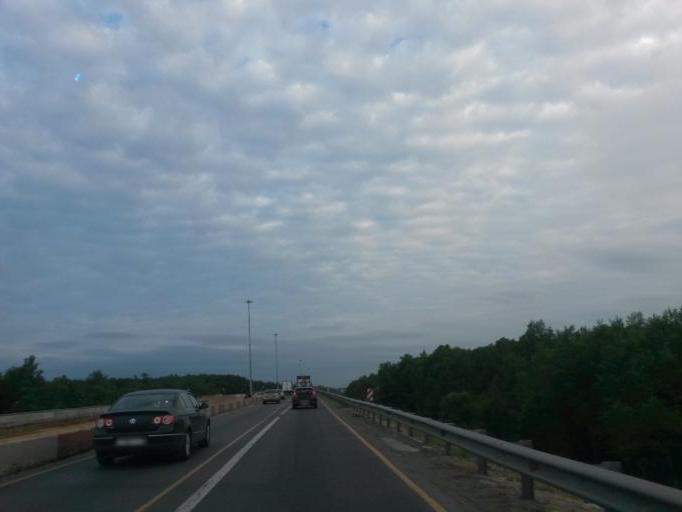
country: RU
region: Moskovskaya
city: Lyubuchany
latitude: 55.2105
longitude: 37.5348
